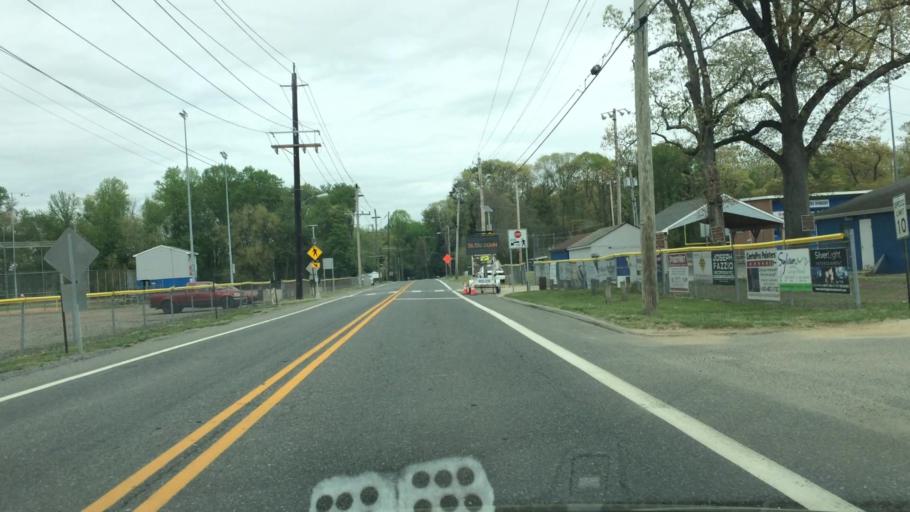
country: US
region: New Jersey
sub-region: Gloucester County
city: Turnersville
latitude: 39.7654
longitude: -75.0798
